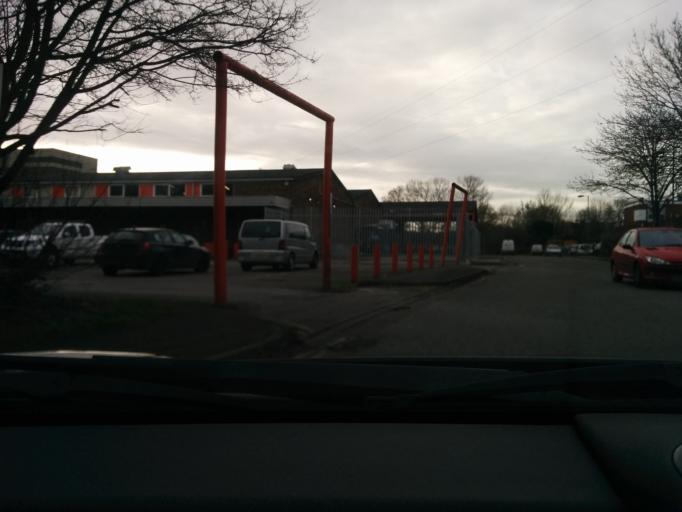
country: GB
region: England
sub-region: Oxfordshire
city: Oxford
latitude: 51.7483
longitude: -1.2753
